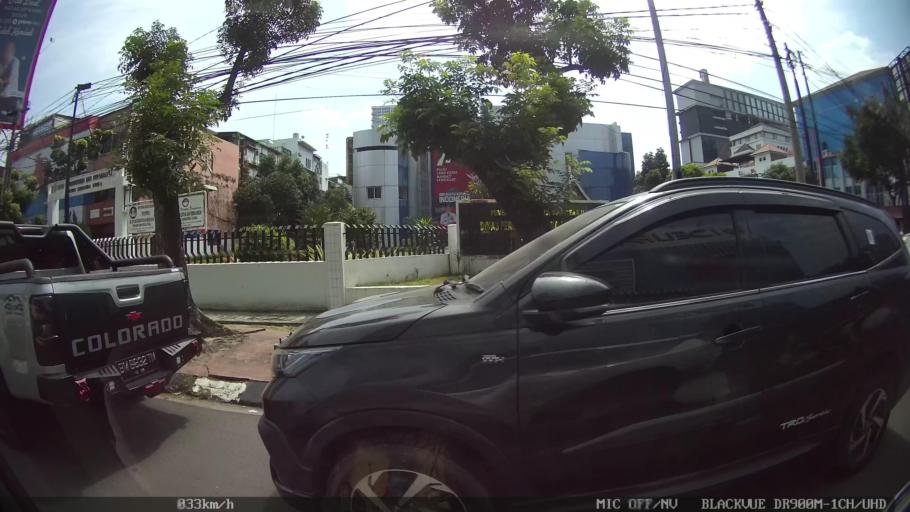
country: ID
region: North Sumatra
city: Medan
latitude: 3.5946
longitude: 98.6761
